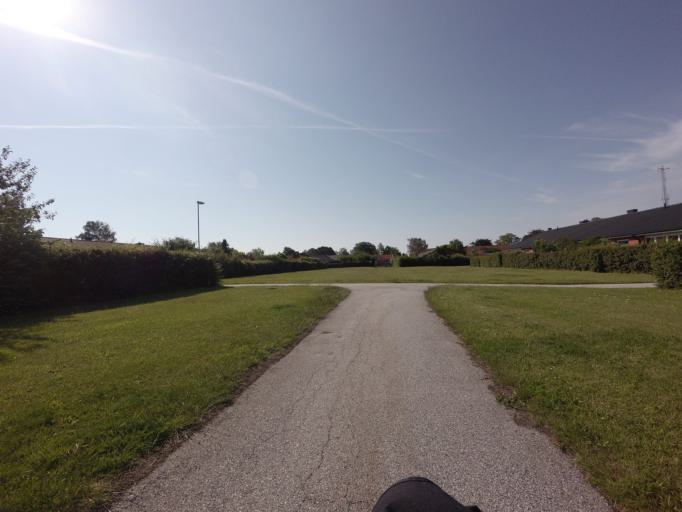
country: SE
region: Skane
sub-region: Malmo
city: Oxie
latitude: 55.4914
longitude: 13.1103
